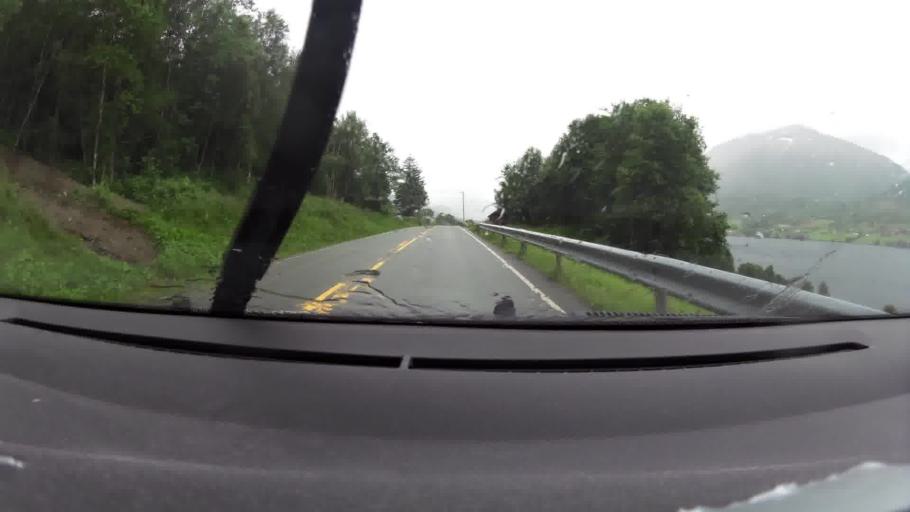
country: NO
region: More og Romsdal
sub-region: Gjemnes
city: Batnfjordsora
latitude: 62.9040
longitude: 7.7063
